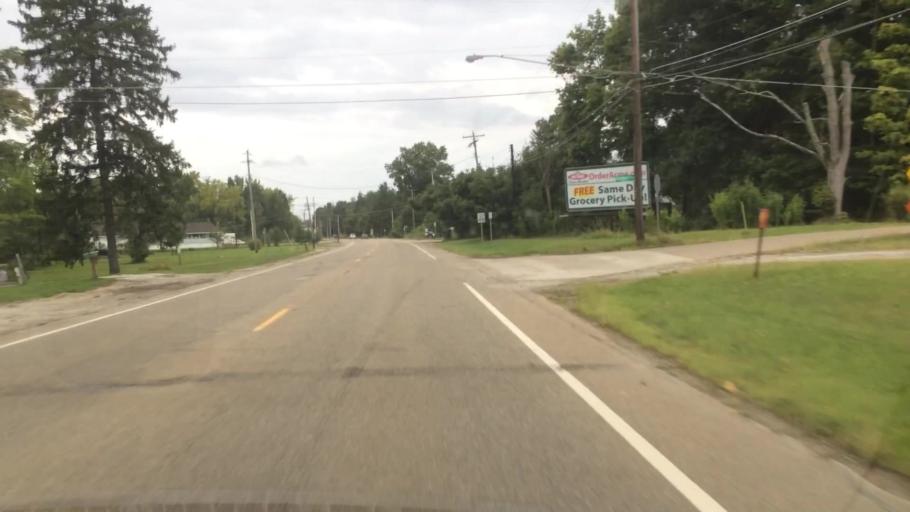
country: US
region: Ohio
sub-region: Summit County
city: Boston Heights
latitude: 41.2102
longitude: -81.4922
